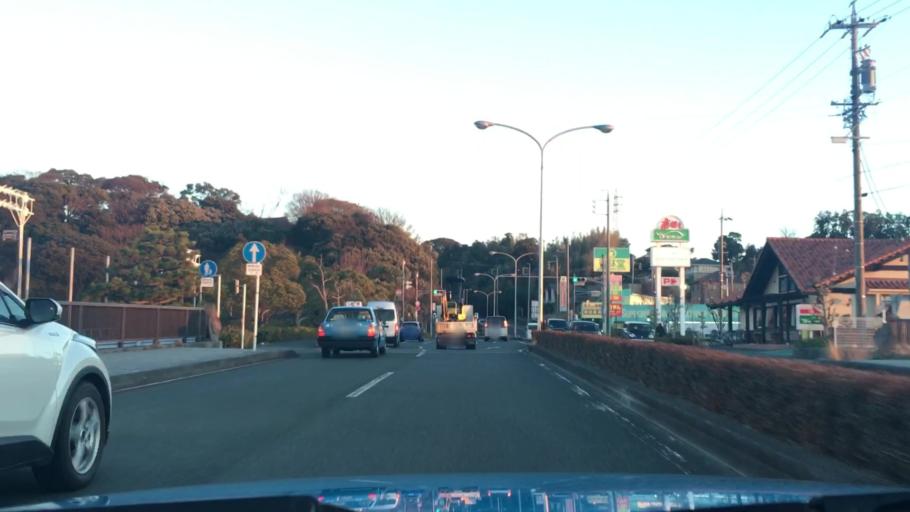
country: JP
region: Shizuoka
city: Hamamatsu
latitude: 34.7218
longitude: 137.7007
